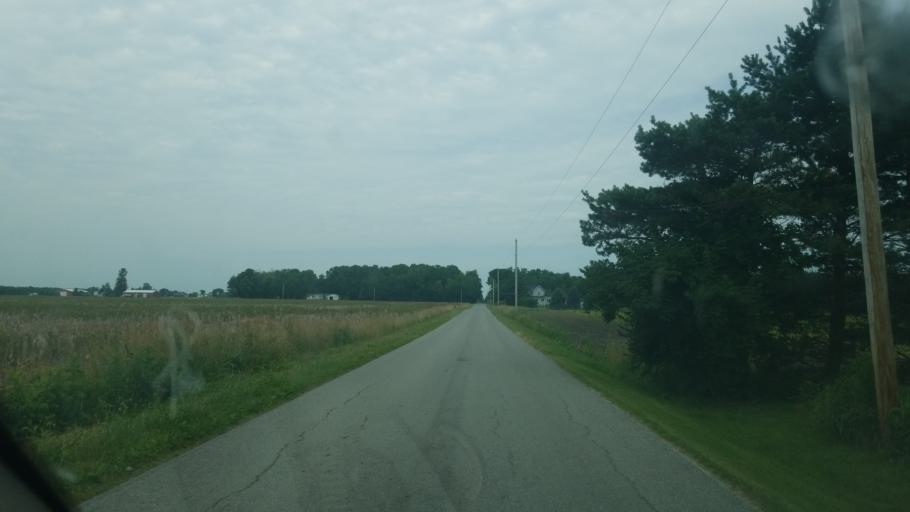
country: US
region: Ohio
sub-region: Seneca County
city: Fostoria
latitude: 41.0502
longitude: -83.4526
